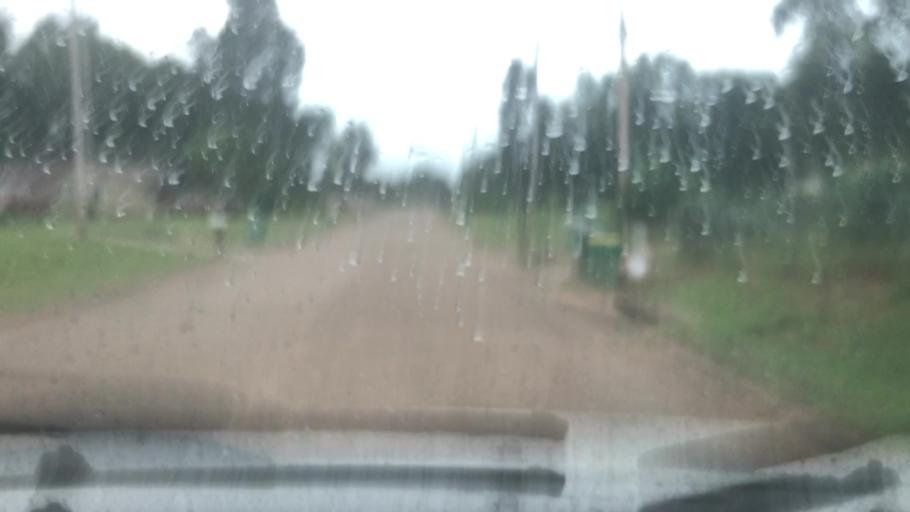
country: US
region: Texas
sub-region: Bowie County
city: Wake Village
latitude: 33.3905
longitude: -94.0856
